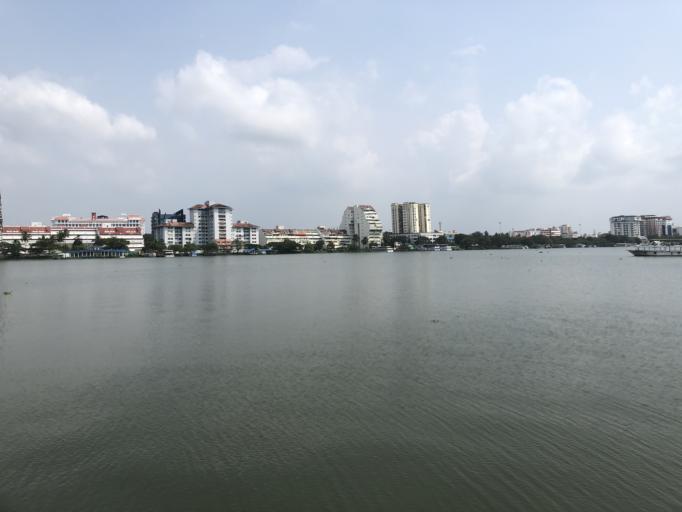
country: IN
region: Kerala
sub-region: Ernakulam
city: Cochin
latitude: 9.9846
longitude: 76.2685
